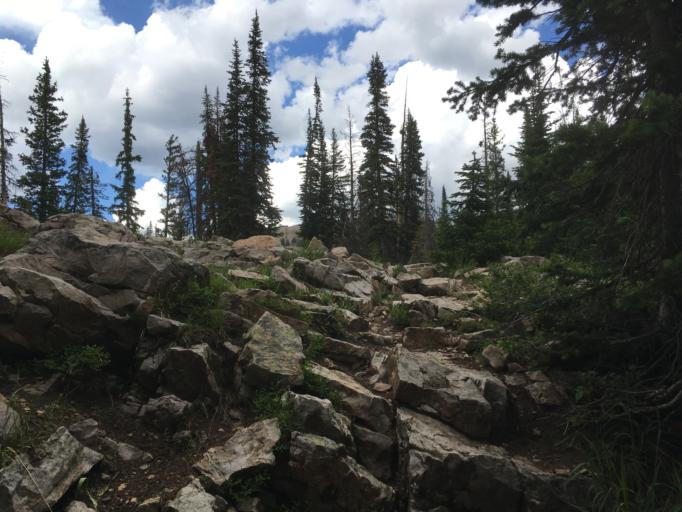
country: US
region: Utah
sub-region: Summit County
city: Kamas
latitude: 40.7184
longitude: -110.8831
